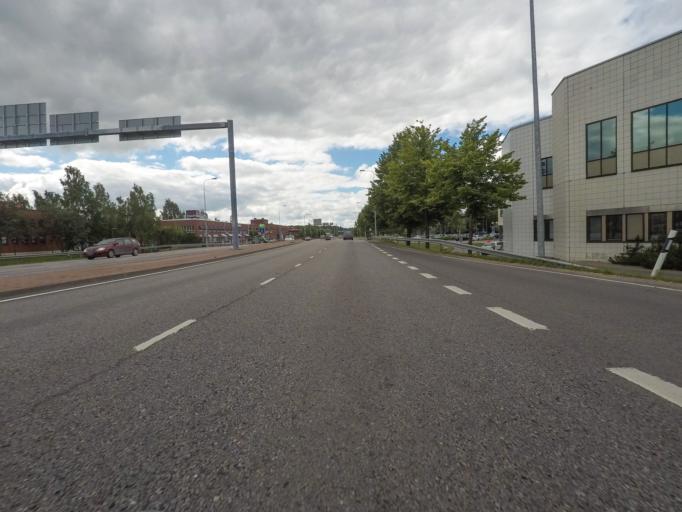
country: FI
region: Varsinais-Suomi
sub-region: Turku
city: Raisio
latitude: 60.4855
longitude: 22.1683
